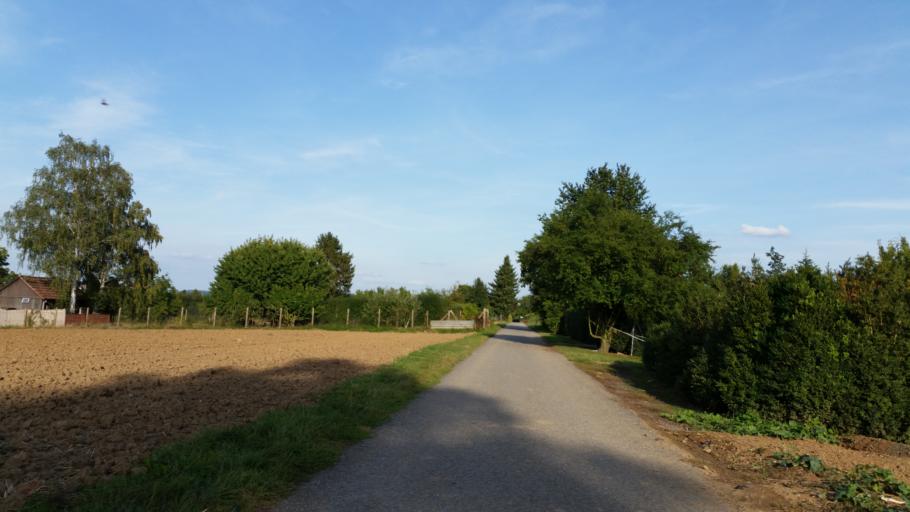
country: DE
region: Baden-Wuerttemberg
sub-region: Regierungsbezirk Stuttgart
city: Ludwigsburg
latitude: 48.8836
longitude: 9.2202
